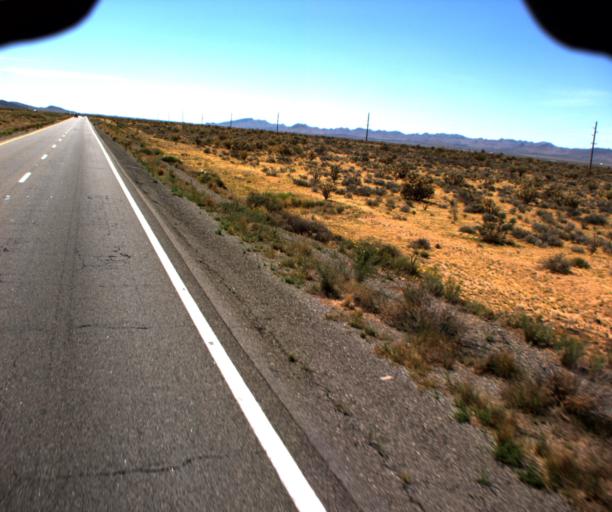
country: US
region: Arizona
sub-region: Mohave County
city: Dolan Springs
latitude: 35.5085
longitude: -114.3381
